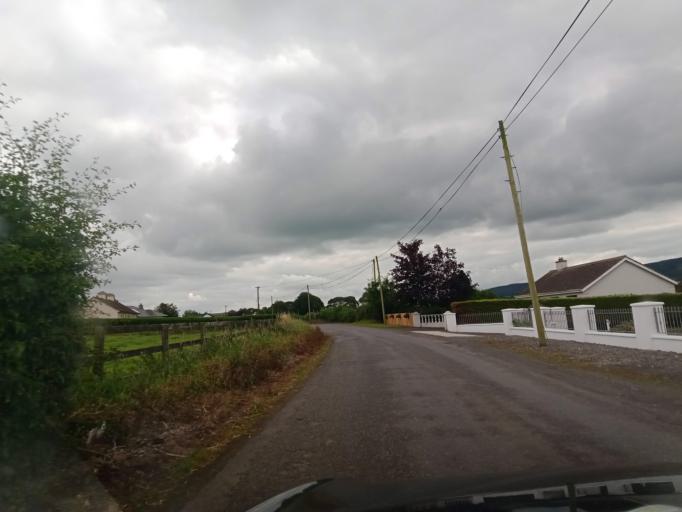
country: IE
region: Leinster
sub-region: Laois
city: Stradbally
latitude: 52.9792
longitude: -7.1628
